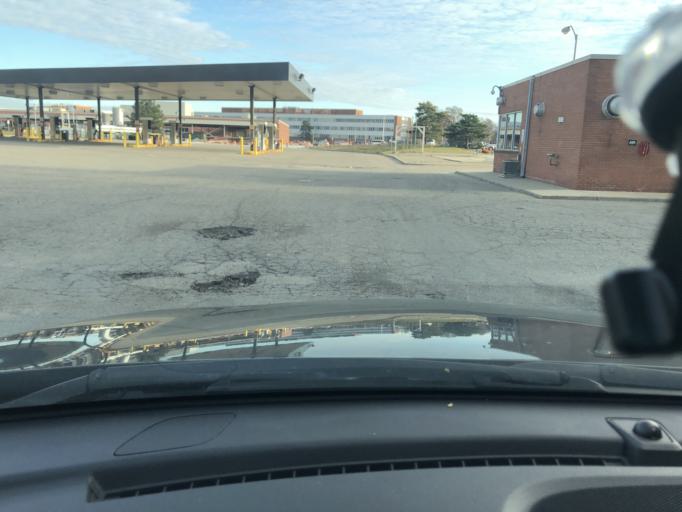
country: US
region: Michigan
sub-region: Wayne County
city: Allen Park
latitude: 42.2948
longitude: -83.2348
